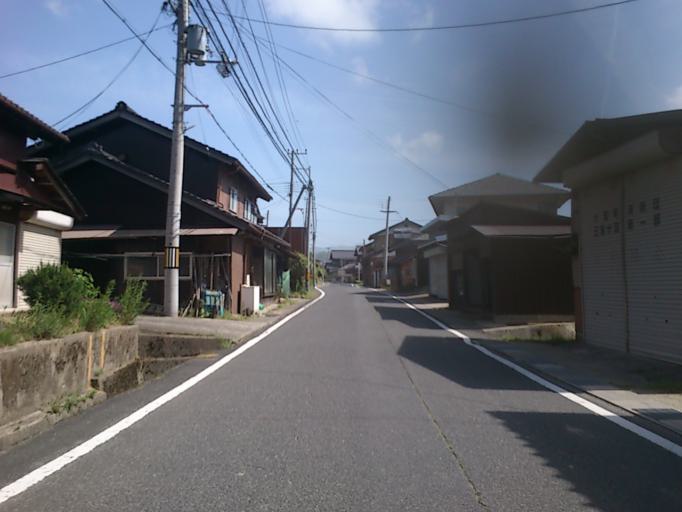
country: JP
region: Kyoto
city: Miyazu
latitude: 35.5663
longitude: 135.1147
